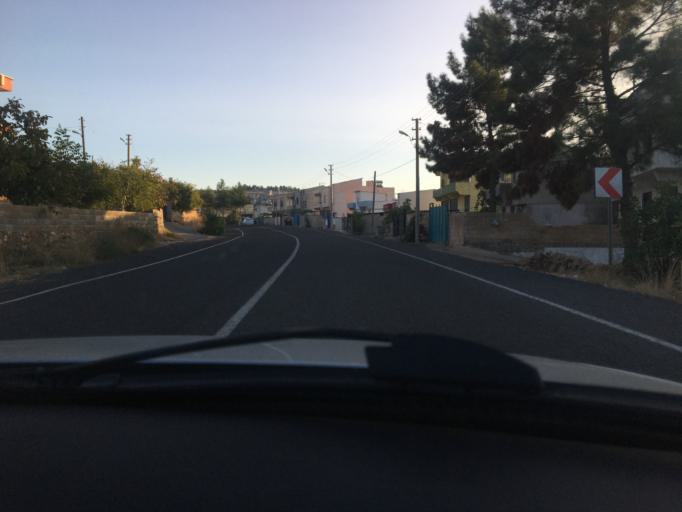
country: TR
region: Sanliurfa
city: Halfeti
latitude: 37.2190
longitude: 37.9543
